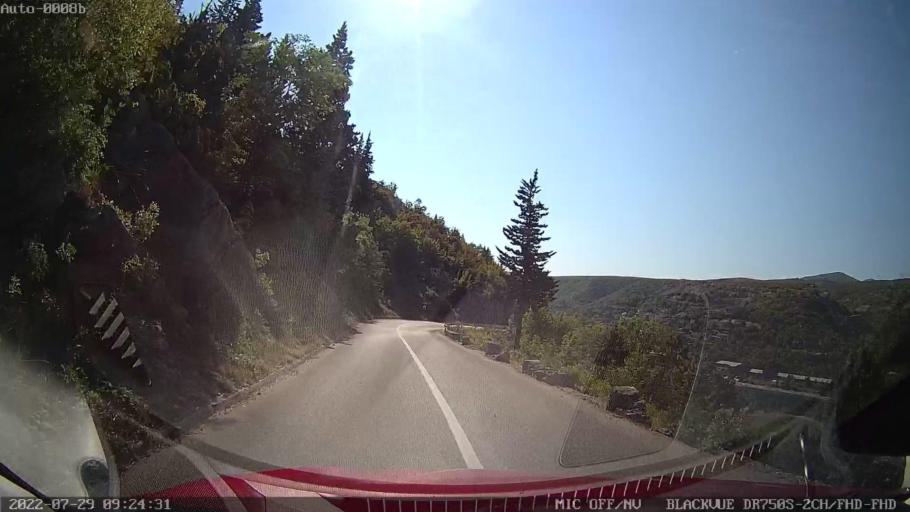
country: HR
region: Zadarska
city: Obrovac
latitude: 44.2026
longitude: 15.6753
